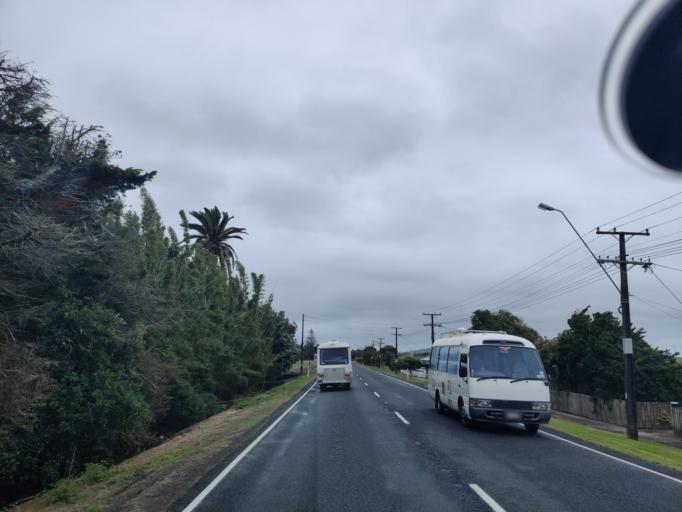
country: NZ
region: Northland
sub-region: Kaipara District
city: Dargaville
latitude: -36.1307
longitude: 174.0327
